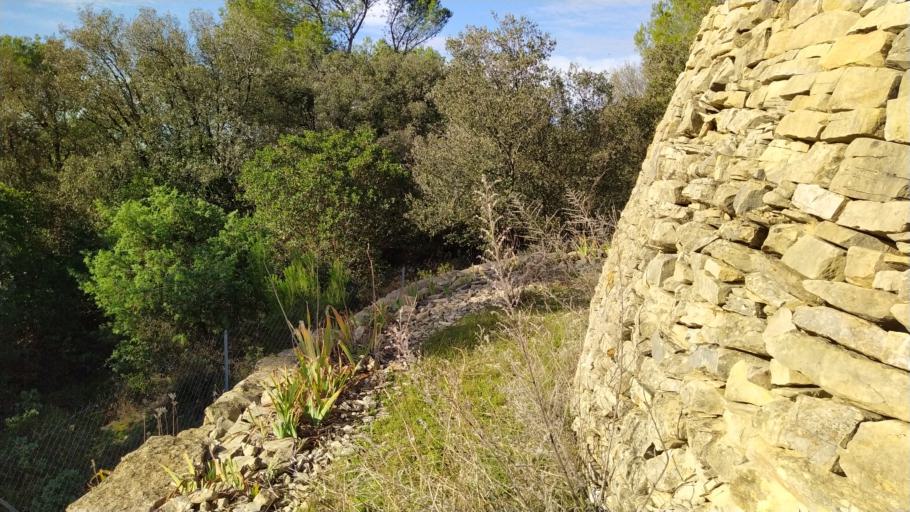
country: FR
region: Languedoc-Roussillon
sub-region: Departement du Gard
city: Poulx
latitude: 43.8719
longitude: 4.4027
